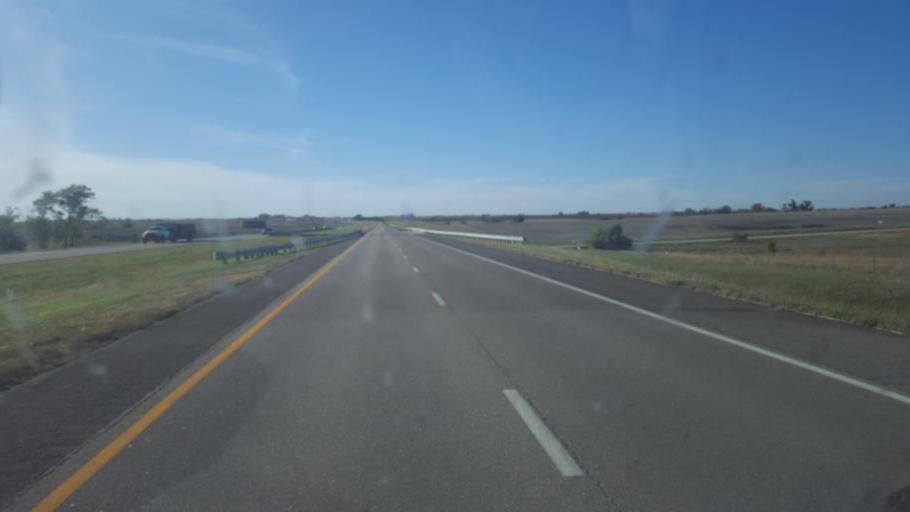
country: US
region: Kansas
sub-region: Ellis County
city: Victoria
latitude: 38.8737
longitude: -99.1126
